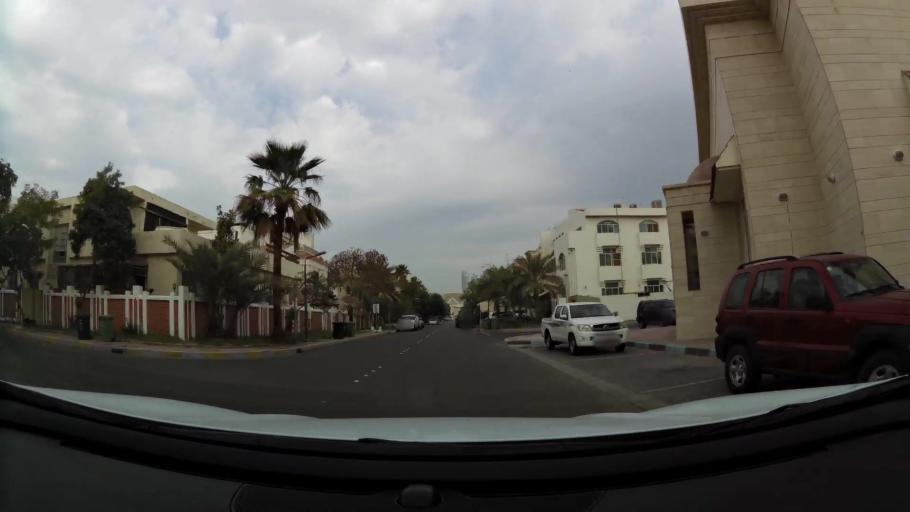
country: AE
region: Abu Dhabi
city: Abu Dhabi
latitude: 24.4637
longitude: 54.3697
